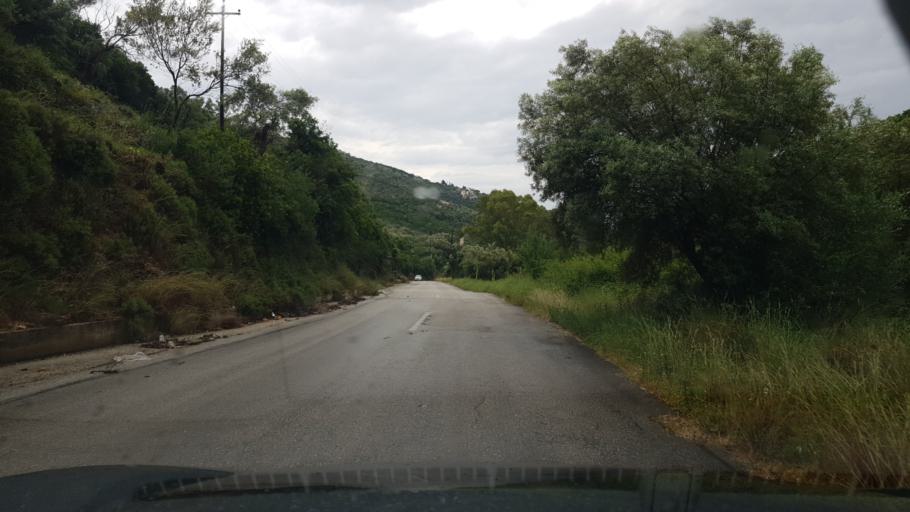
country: GR
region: Ionian Islands
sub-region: Lefkada
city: Nidri
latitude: 38.6306
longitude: 20.6733
